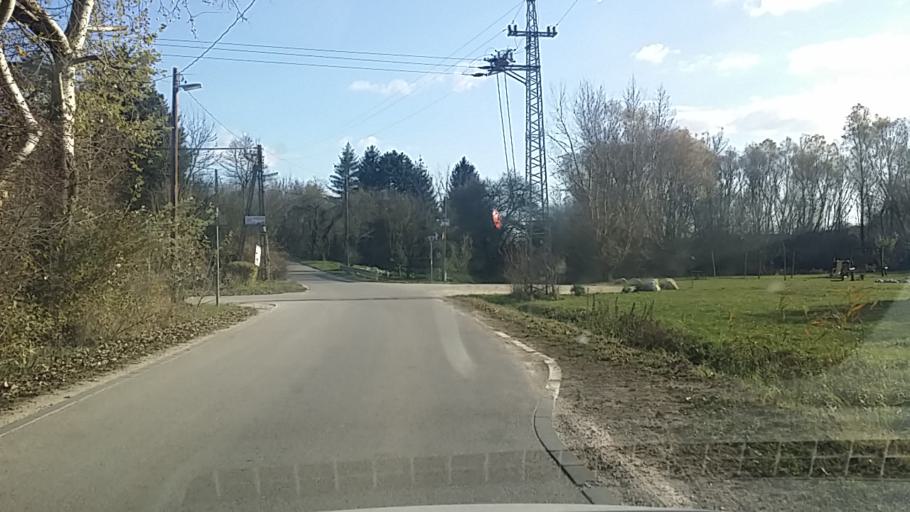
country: HU
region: Pest
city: Pilisszanto
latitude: 47.6483
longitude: 18.9079
